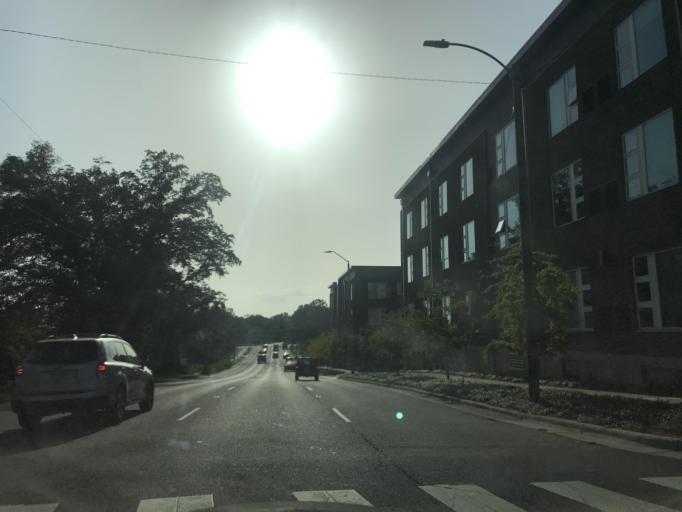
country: US
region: North Carolina
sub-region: New Hanover County
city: Wilmington
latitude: 34.2257
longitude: -77.9422
